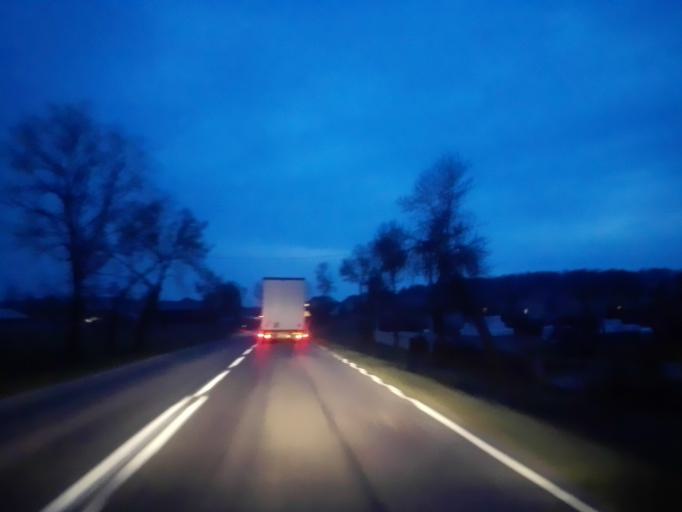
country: PL
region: Podlasie
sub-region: Powiat lomzynski
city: Sniadowo
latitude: 53.0626
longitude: 22.0035
